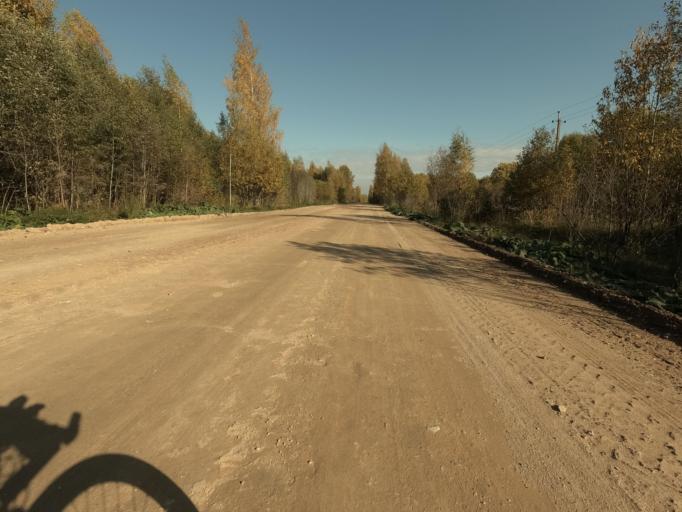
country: RU
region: Novgorod
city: Batetskiy
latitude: 58.8294
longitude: 30.7131
